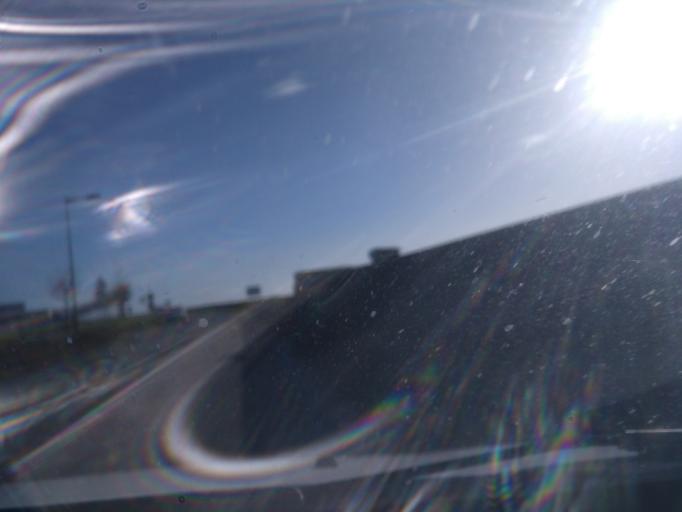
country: FR
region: Brittany
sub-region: Departement d'Ille-et-Vilaine
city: Pleine-Fougeres
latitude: 48.5331
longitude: -1.5576
